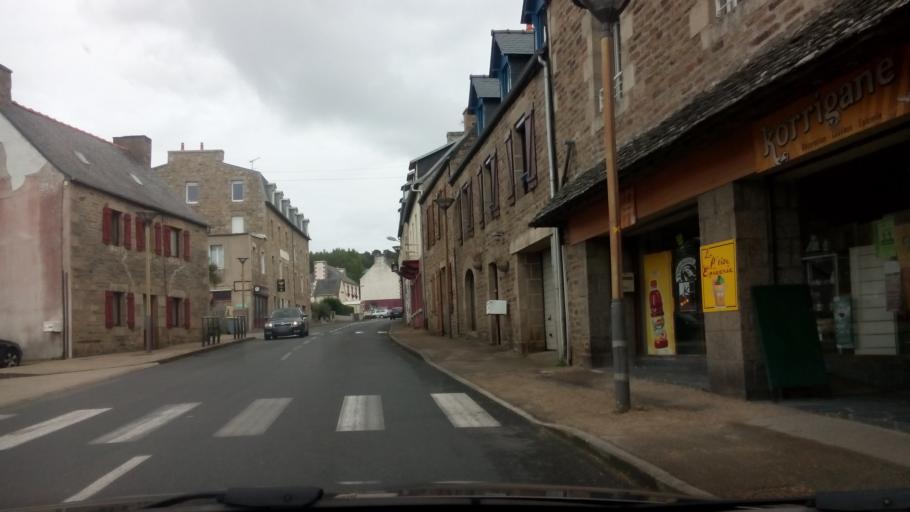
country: FR
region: Brittany
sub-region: Departement des Cotes-d'Armor
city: Locquemeau
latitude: 48.6844
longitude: -3.5666
